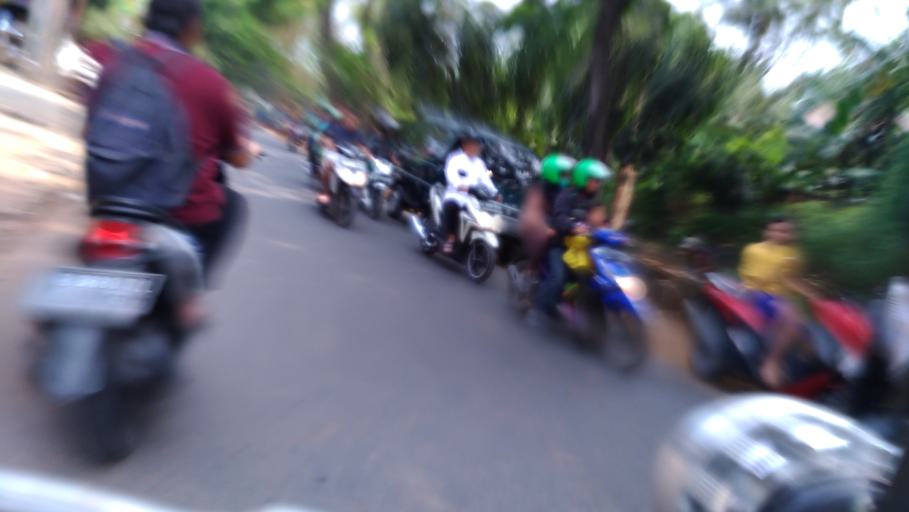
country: ID
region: West Java
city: Depok
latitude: -6.3513
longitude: 106.8785
